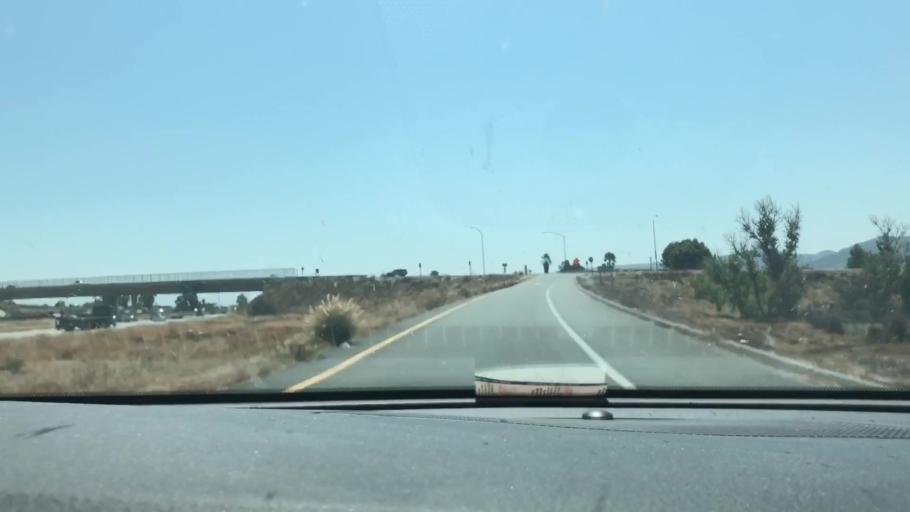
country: US
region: California
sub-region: Riverside County
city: Wildomar
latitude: 33.6141
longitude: -117.2627
